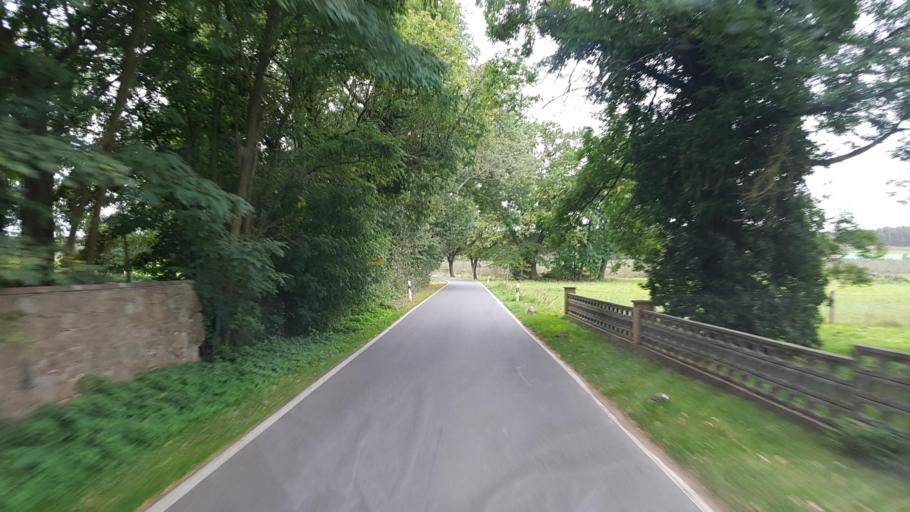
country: DE
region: Brandenburg
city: Drahnsdorf
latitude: 51.9578
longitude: 13.5425
